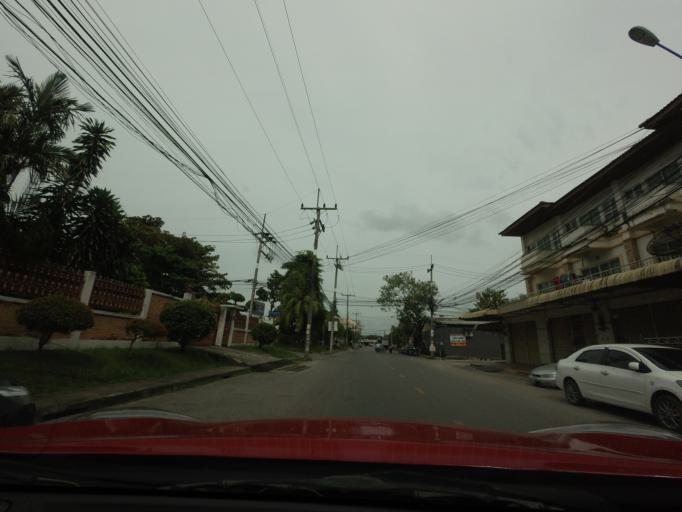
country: TH
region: Songkhla
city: Hat Yai
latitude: 6.9899
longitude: 100.4816
